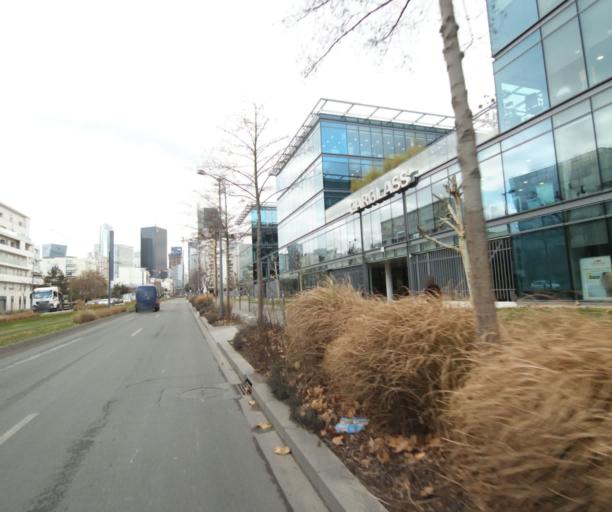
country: FR
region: Ile-de-France
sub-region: Departement des Hauts-de-Seine
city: La Garenne-Colombes
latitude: 48.9019
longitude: 2.2395
